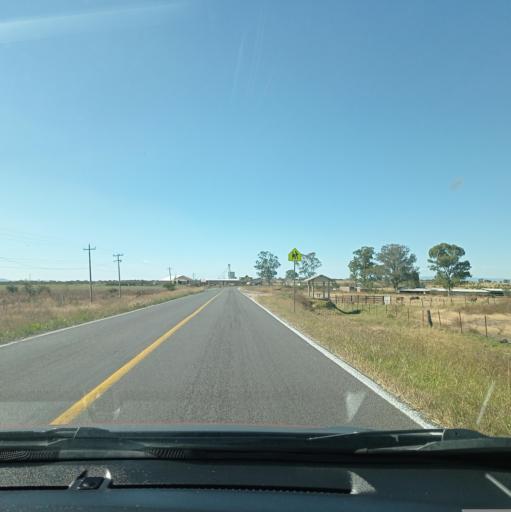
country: MX
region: Jalisco
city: Valle de Guadalupe
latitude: 21.0231
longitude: -102.5429
